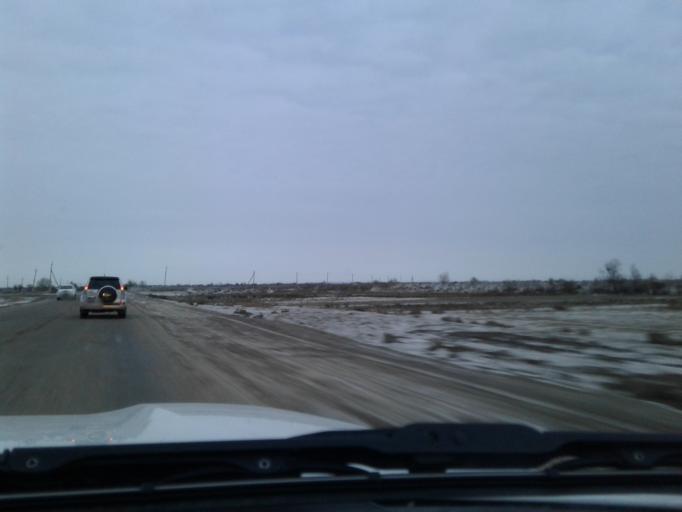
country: UZ
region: Karakalpakstan
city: Manghit
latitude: 42.0162
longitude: 59.8944
